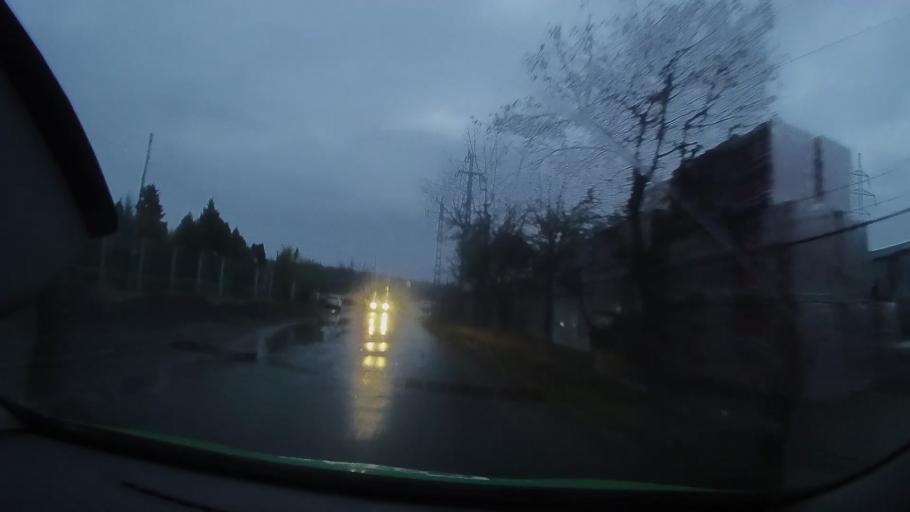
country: RO
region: Mures
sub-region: Municipiul Reghin
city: Iernuteni
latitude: 46.7665
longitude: 24.7224
